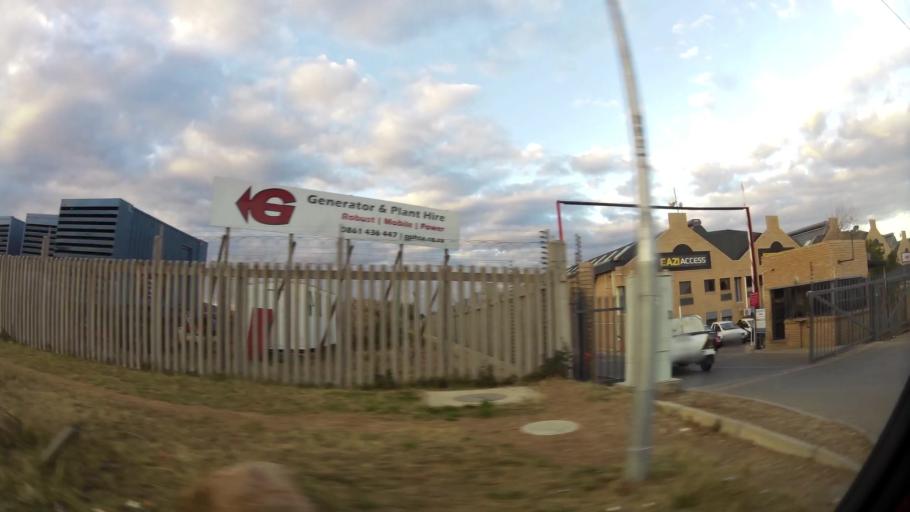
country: ZA
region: Gauteng
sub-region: City of Johannesburg Metropolitan Municipality
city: Midrand
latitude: -26.0002
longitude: 28.1407
